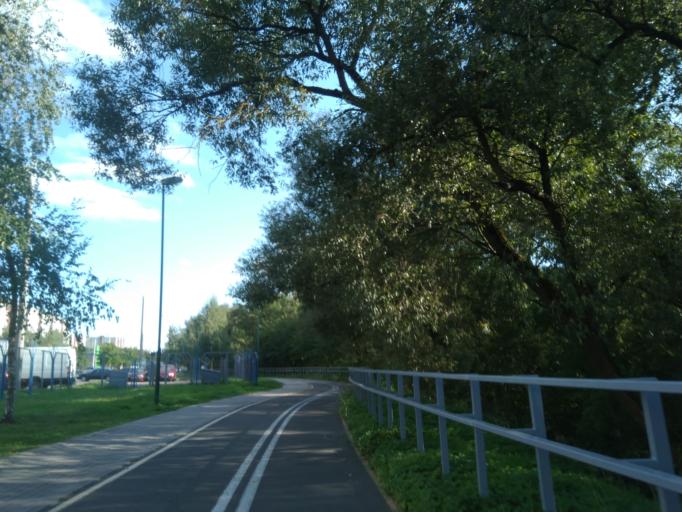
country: BY
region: Minsk
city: Minsk
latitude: 53.8650
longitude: 27.5845
